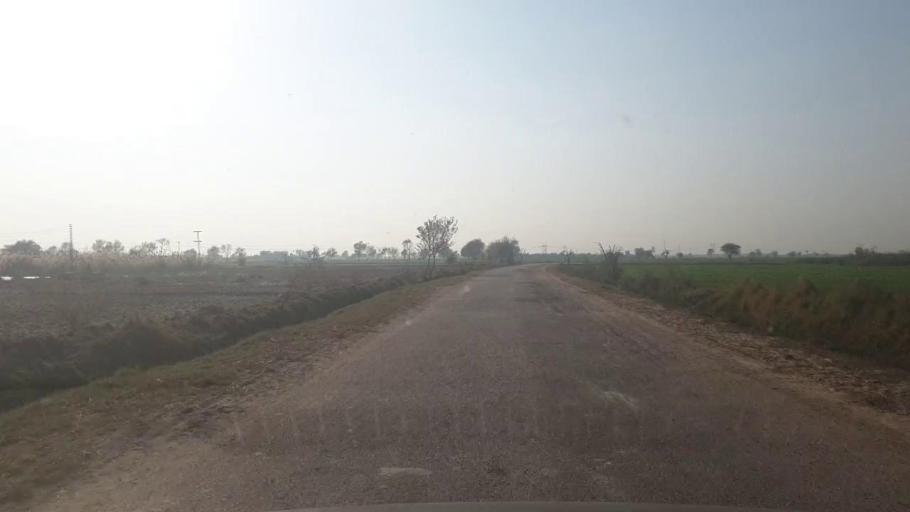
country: PK
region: Sindh
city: Sakrand
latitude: 26.0514
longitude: 68.3684
